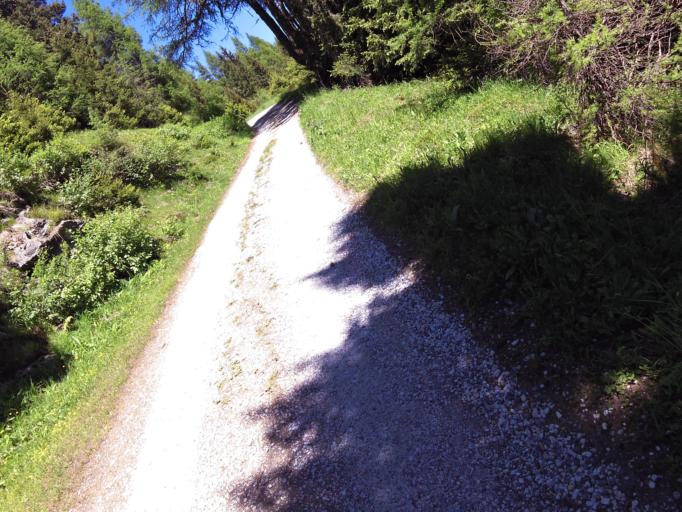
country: AT
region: Tyrol
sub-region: Politischer Bezirk Innsbruck Land
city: Neustift im Stubaital
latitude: 47.1227
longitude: 11.2917
